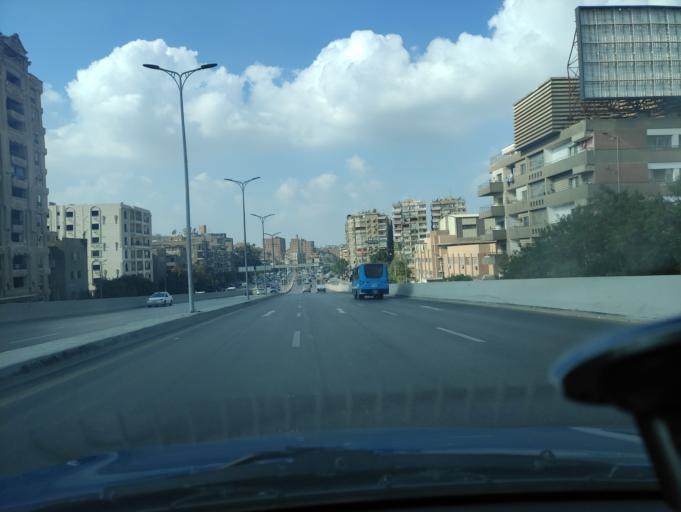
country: EG
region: Muhafazat al Qahirah
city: Cairo
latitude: 30.1041
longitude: 31.3279
